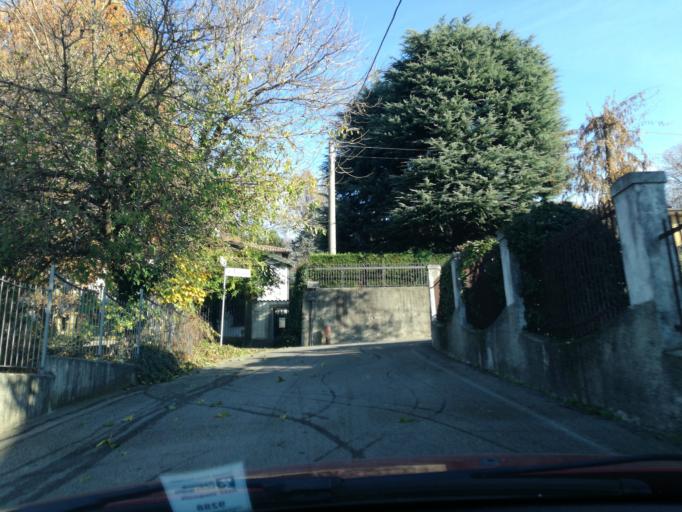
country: IT
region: Lombardy
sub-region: Provincia di Lecco
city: Robbiate
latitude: 45.7010
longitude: 9.4304
